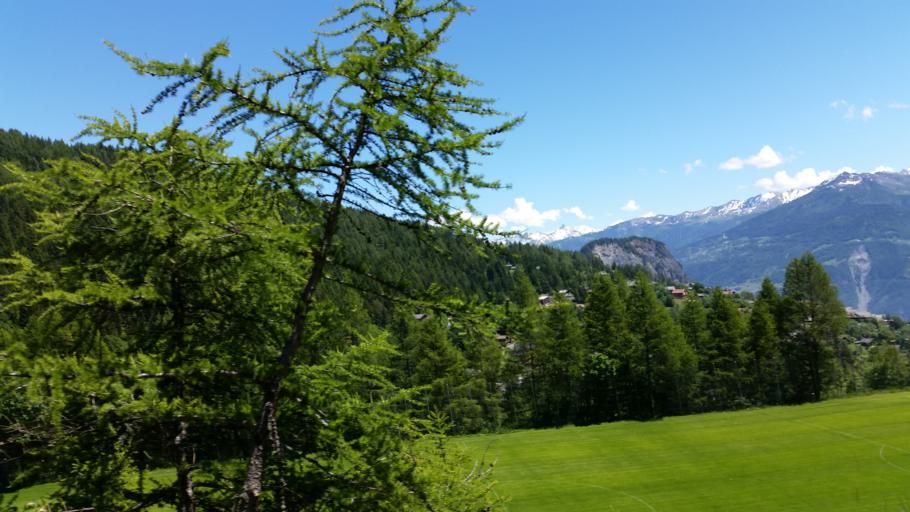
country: CH
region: Valais
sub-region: Martigny District
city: Saillon
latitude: 46.2037
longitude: 7.1614
